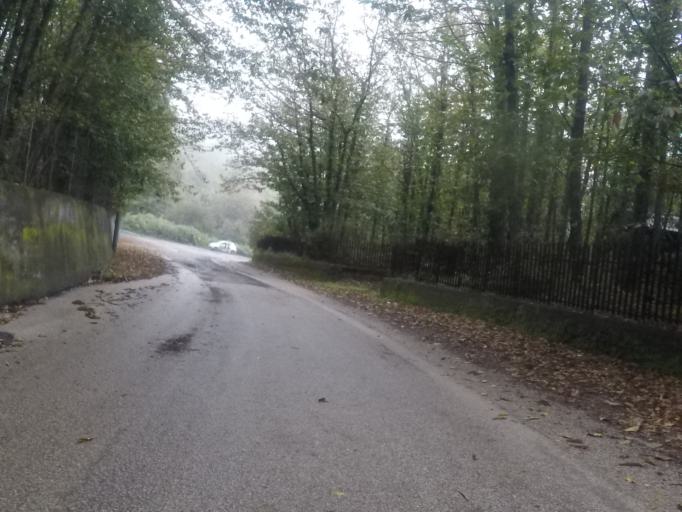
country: IT
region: Sicily
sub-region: Catania
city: Nicolosi
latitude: 37.6622
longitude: 15.0375
